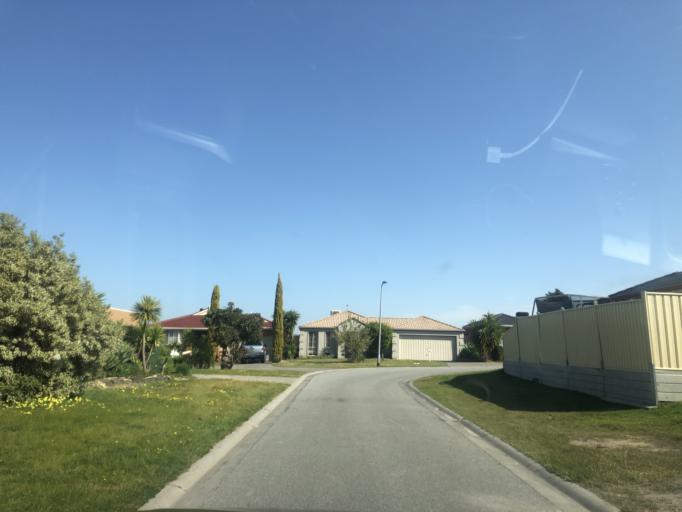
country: AU
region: Victoria
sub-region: Casey
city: Lynbrook
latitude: -38.0460
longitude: 145.2722
